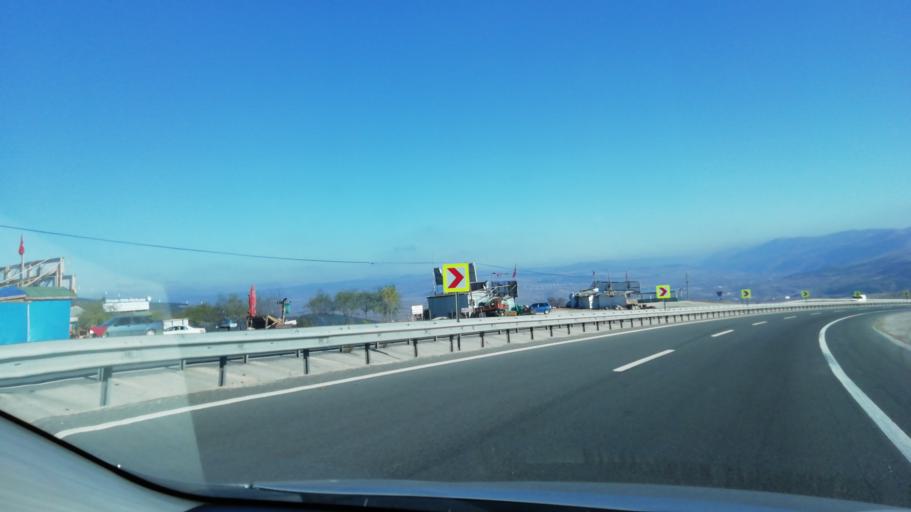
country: TR
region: Karabuk
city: Gozyeri
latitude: 40.8636
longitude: 32.5517
